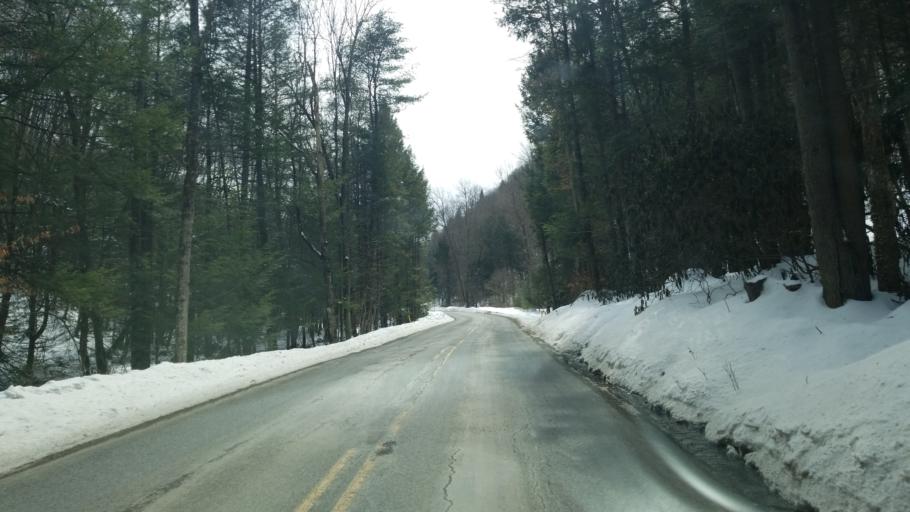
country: US
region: Pennsylvania
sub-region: Clearfield County
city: Shiloh
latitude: 41.2572
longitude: -78.1520
